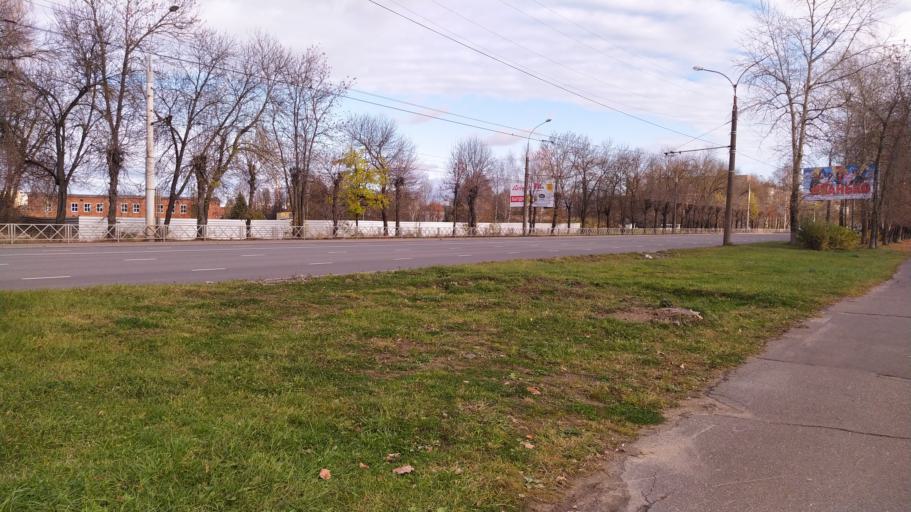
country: RU
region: Jaroslavl
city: Rybinsk
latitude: 58.0567
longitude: 38.7909
